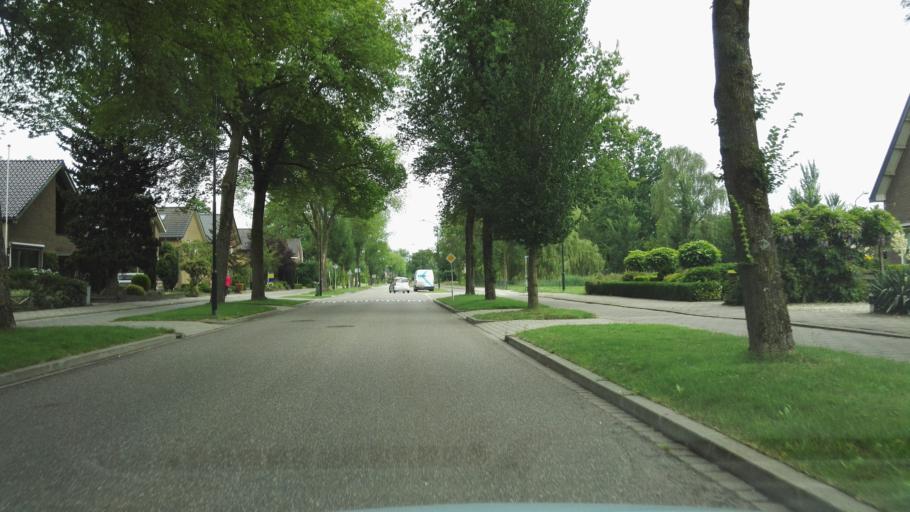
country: NL
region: Gelderland
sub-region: Gemeente Apeldoorn
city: Apeldoorn
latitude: 52.2317
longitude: 5.9906
